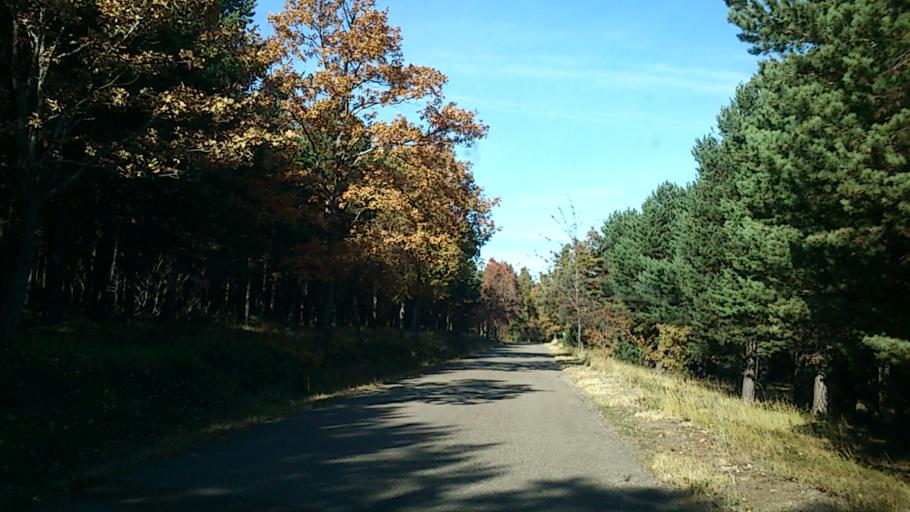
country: ES
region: Aragon
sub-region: Provincia de Zaragoza
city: Litago
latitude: 41.8053
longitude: -1.7925
